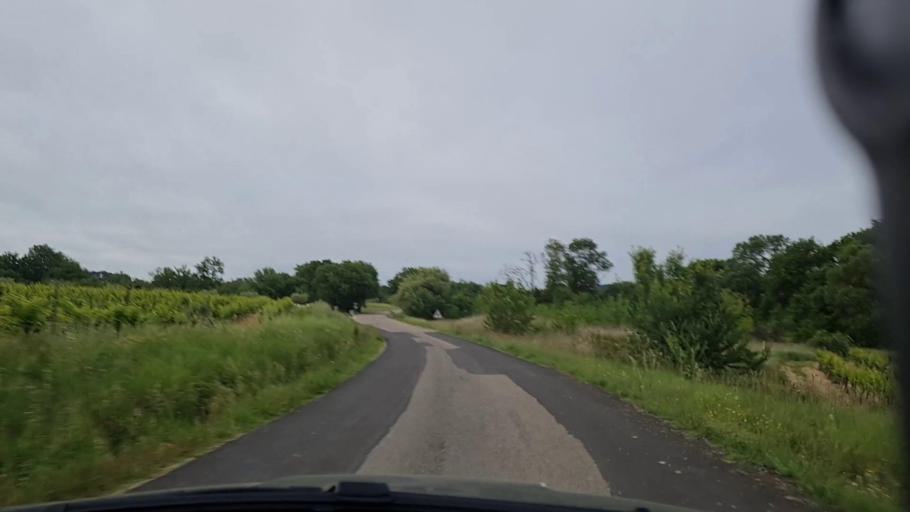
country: FR
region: Languedoc-Roussillon
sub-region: Departement du Gard
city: Villevieille
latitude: 43.8355
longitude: 4.0848
